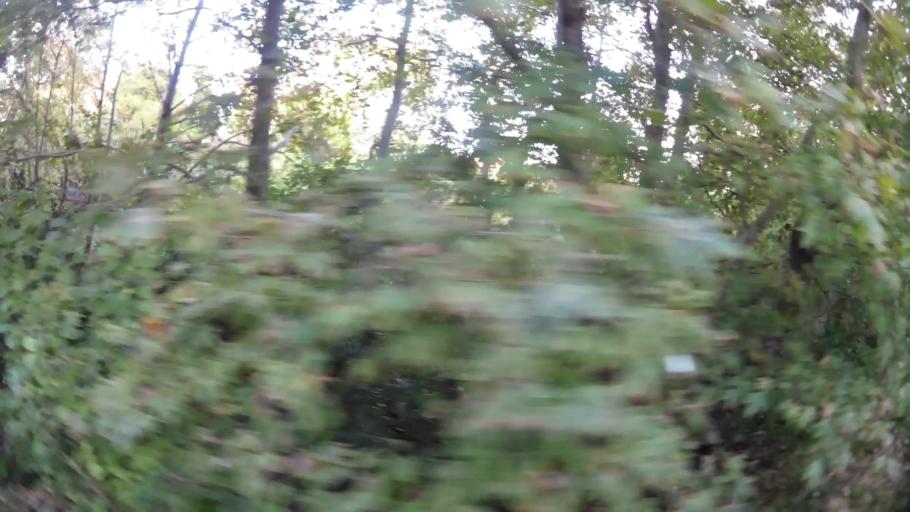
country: GR
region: Attica
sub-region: Nomarchia Anatolikis Attikis
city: Kryoneri
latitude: 38.1427
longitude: 23.8357
